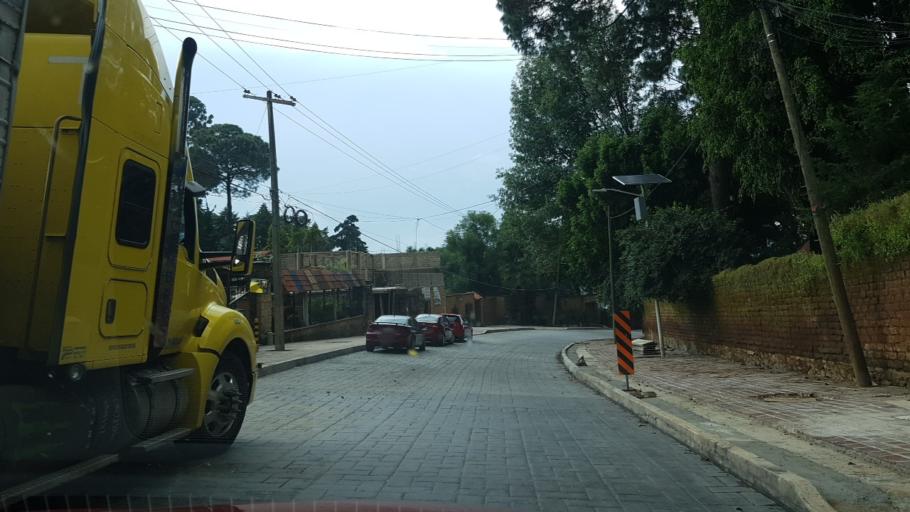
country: MX
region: Mexico
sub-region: Valle de Bravo
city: Casas Viejas
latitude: 19.1649
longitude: -100.1247
